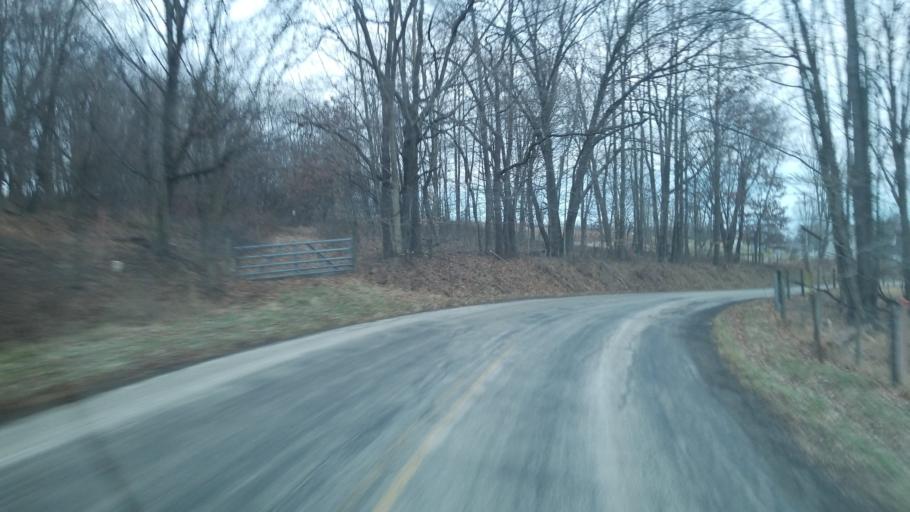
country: US
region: Ohio
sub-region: Holmes County
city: Millersburg
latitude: 40.4894
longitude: -81.8723
